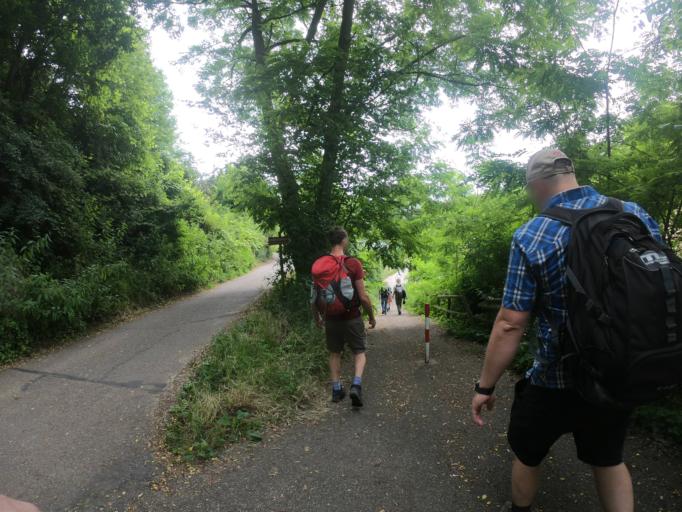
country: DE
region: Rheinland-Pfalz
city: Bad Bergzabern
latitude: 49.1137
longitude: 7.9946
